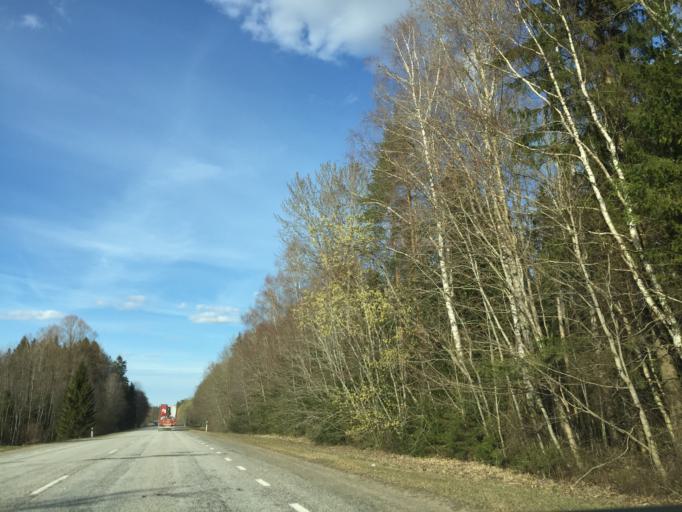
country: EE
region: Tartu
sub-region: Elva linn
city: Elva
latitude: 58.1184
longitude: 26.5146
